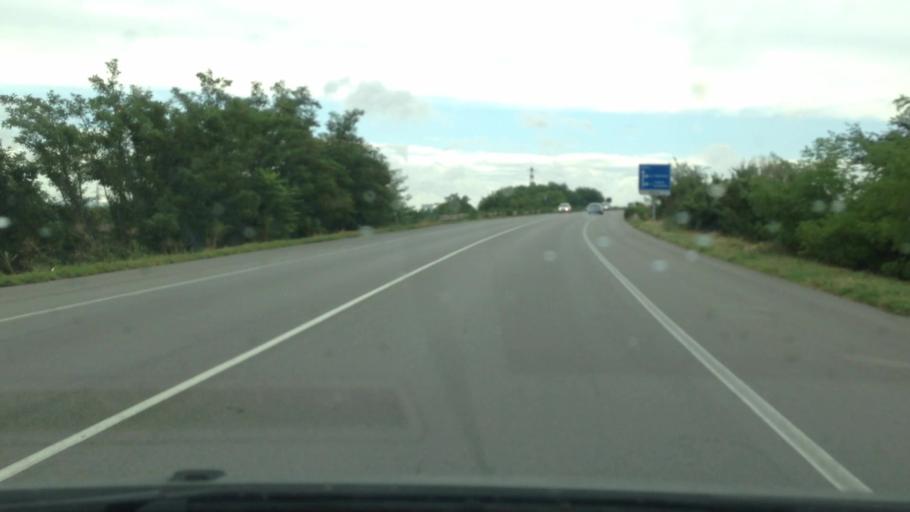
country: IT
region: Piedmont
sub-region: Provincia di Alessandria
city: Tortona
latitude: 44.8992
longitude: 8.8396
